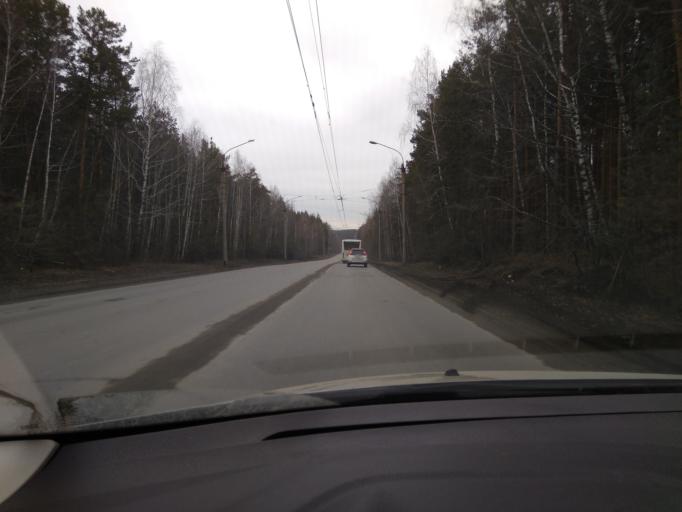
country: RU
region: Chelyabinsk
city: Turgoyak
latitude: 55.1215
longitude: 60.1315
